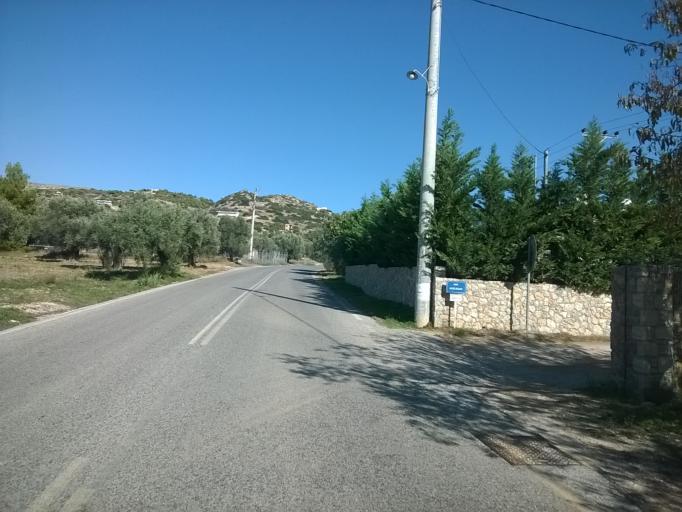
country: GR
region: Attica
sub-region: Nomarchia Anatolikis Attikis
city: Keratea
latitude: 37.7645
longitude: 23.9819
